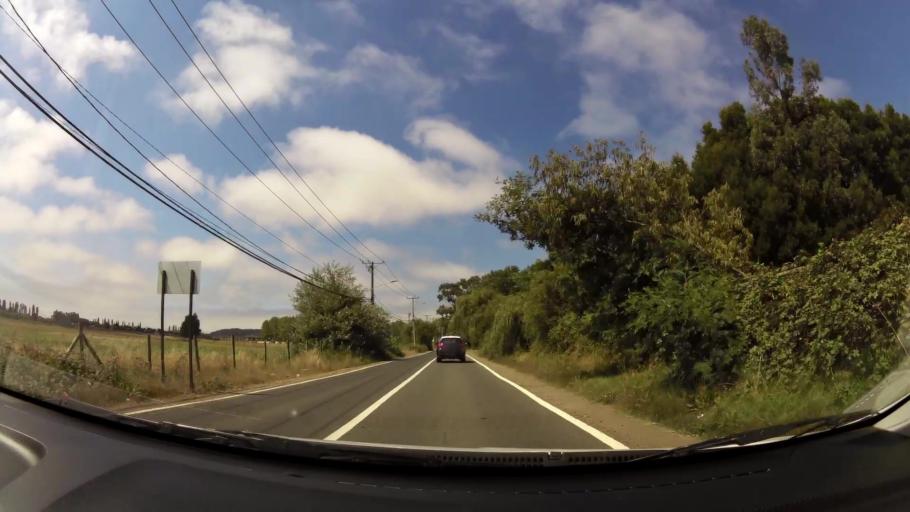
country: CL
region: Biobio
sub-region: Provincia de Concepcion
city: Concepcion
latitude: -36.7775
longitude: -73.0551
